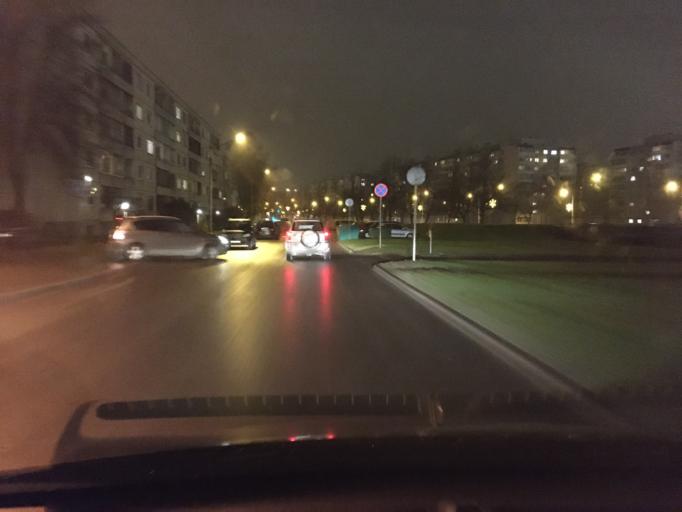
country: EE
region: Harju
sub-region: Tallinna linn
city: Kose
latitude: 59.4340
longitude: 24.8296
